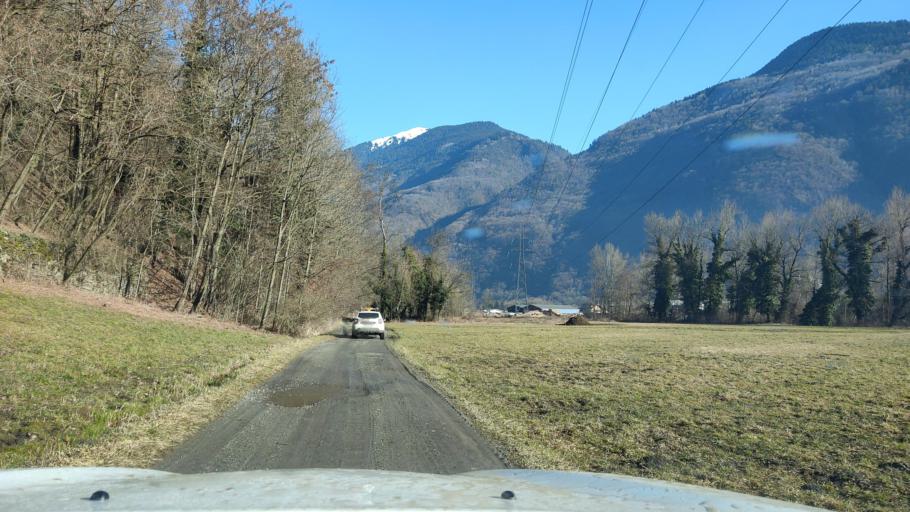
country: FR
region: Rhone-Alpes
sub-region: Departement de la Savoie
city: La Bathie
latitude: 45.6031
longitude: 6.4434
